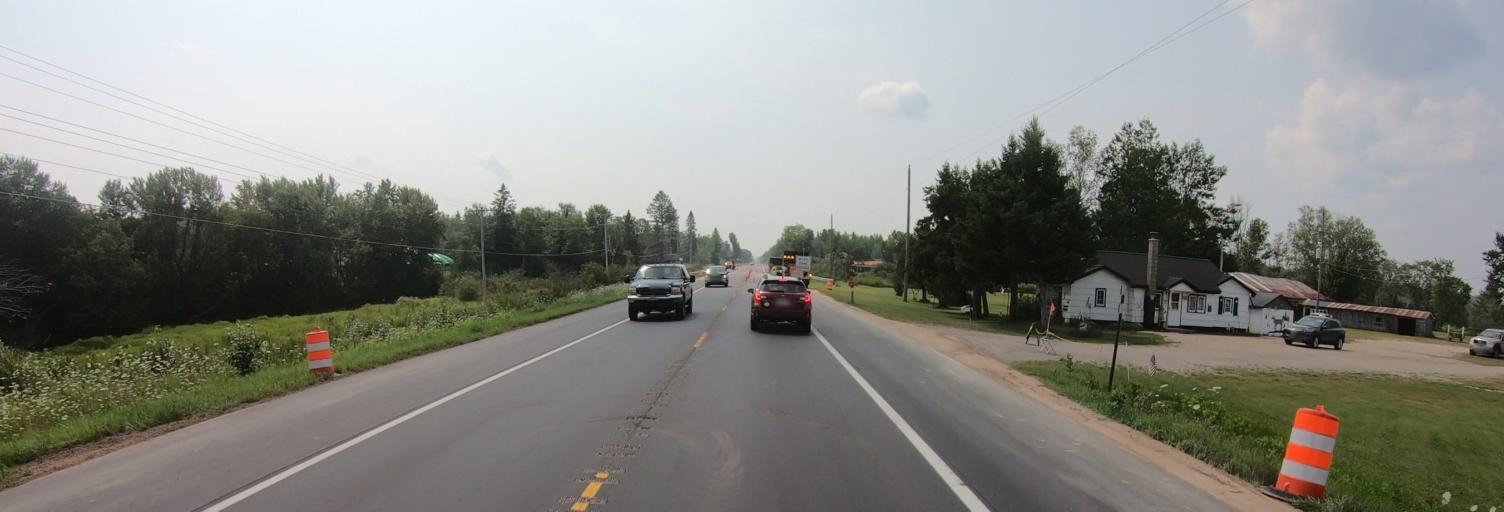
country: US
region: Michigan
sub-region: Luce County
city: Newberry
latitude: 46.3736
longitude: -85.5099
